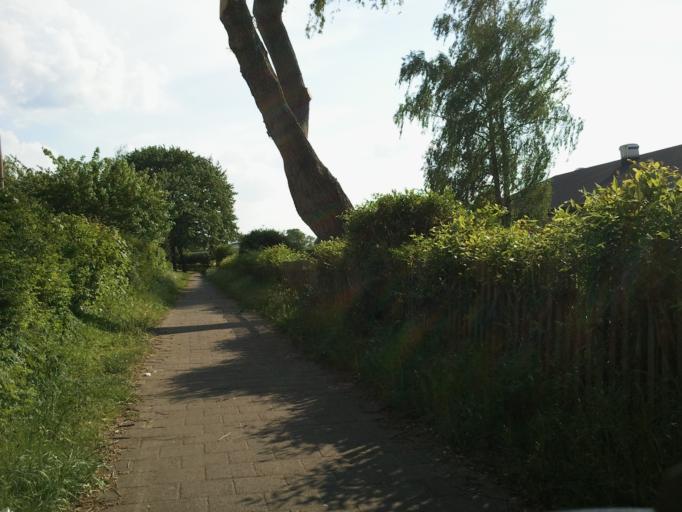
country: DE
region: Lower Saxony
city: Nienburg
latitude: 52.6262
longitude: 9.2269
